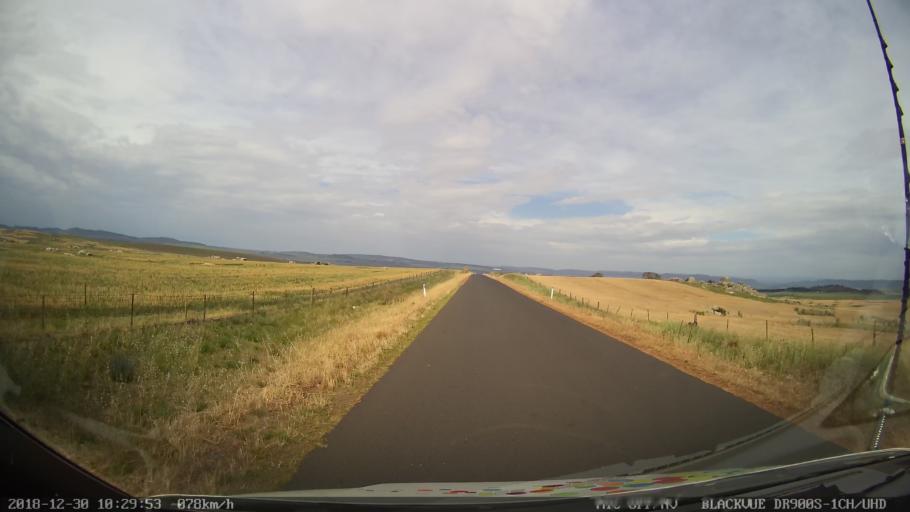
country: AU
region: New South Wales
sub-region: Snowy River
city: Berridale
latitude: -36.5018
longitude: 148.9030
